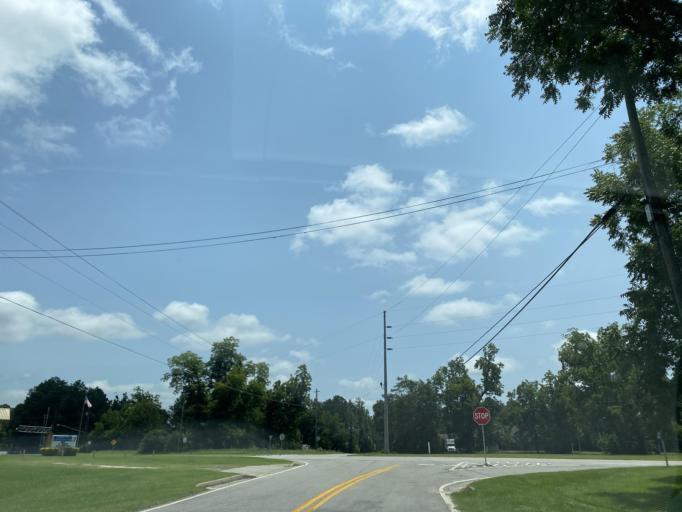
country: US
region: Georgia
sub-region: Telfair County
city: Lumber City
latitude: 31.9375
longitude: -82.6863
